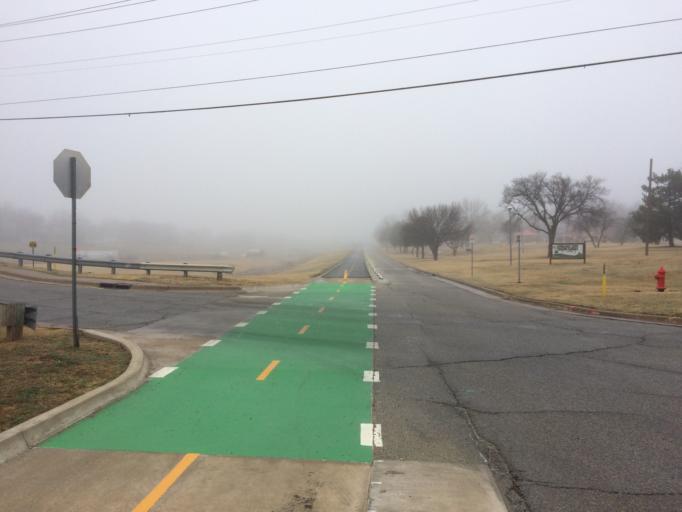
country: US
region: Oklahoma
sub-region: Oklahoma County
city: Warr Acres
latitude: 35.4822
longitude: -97.5768
